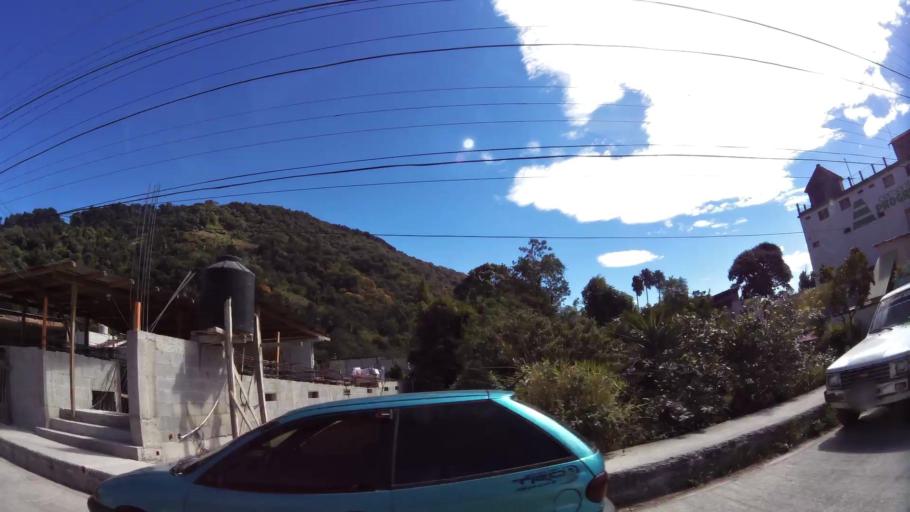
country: GT
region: Solola
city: Panajachel
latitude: 14.7416
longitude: -91.1516
